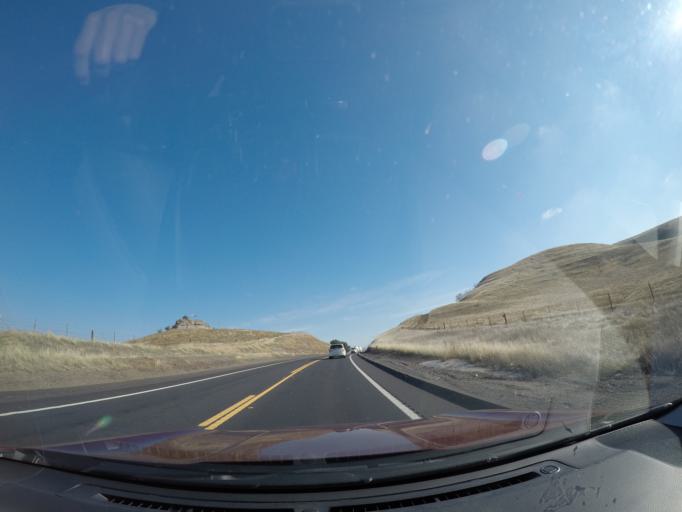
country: US
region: California
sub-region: Stanislaus County
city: East Oakdale
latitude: 37.8068
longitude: -120.6951
